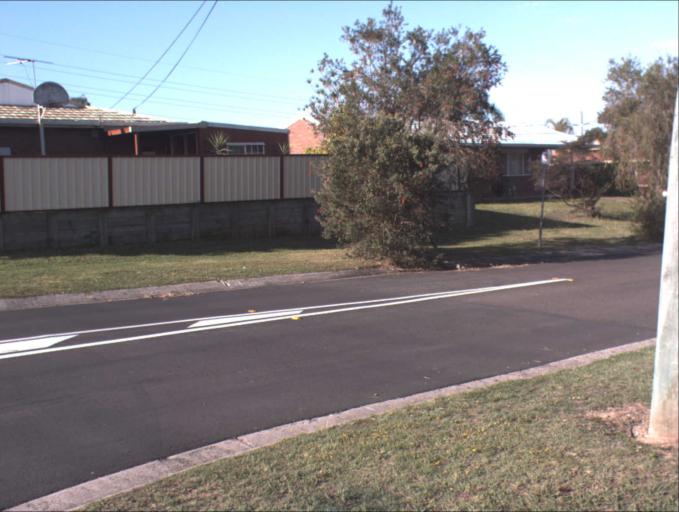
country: AU
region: Queensland
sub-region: Logan
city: Woodridge
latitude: -27.6686
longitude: 153.0558
